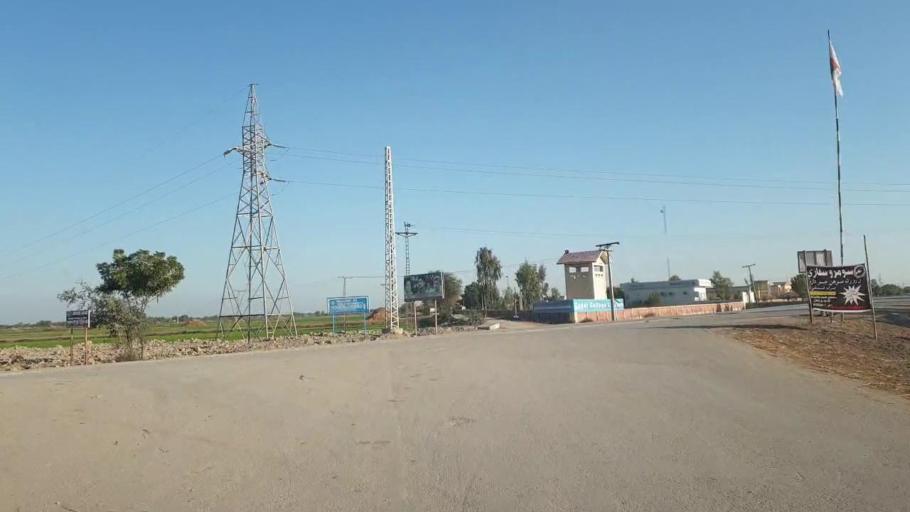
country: PK
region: Sindh
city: Dokri
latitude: 27.3639
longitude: 68.1172
